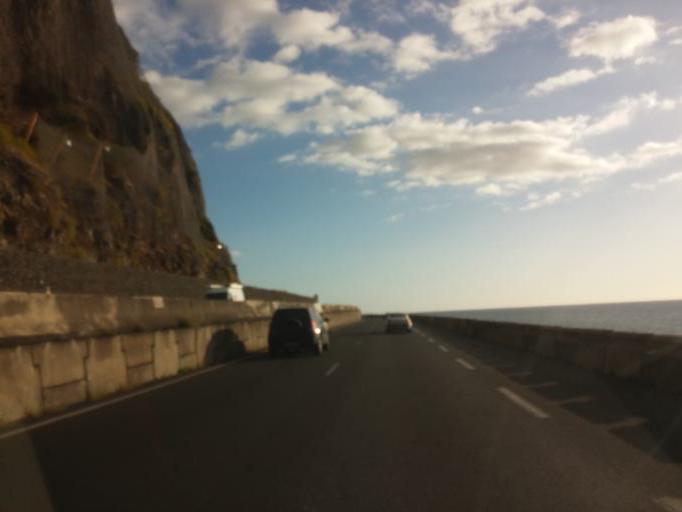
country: RE
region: Reunion
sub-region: Reunion
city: La Possession
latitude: -20.8974
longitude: 55.3728
